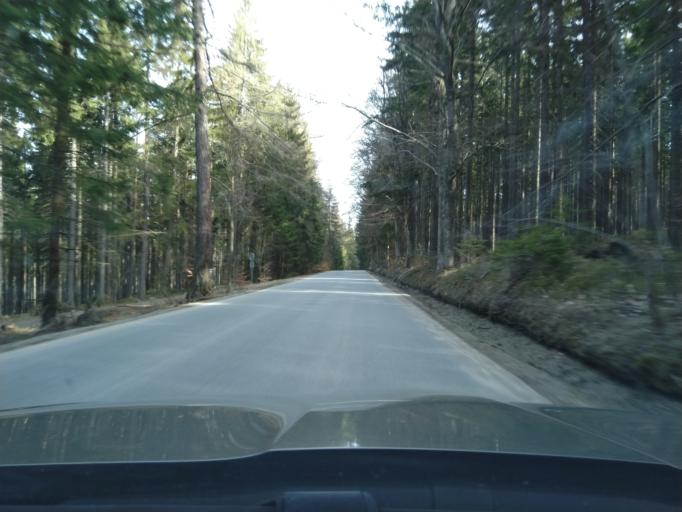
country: CZ
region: Jihocesky
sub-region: Okres Prachatice
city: Stachy
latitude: 49.0682
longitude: 13.6493
